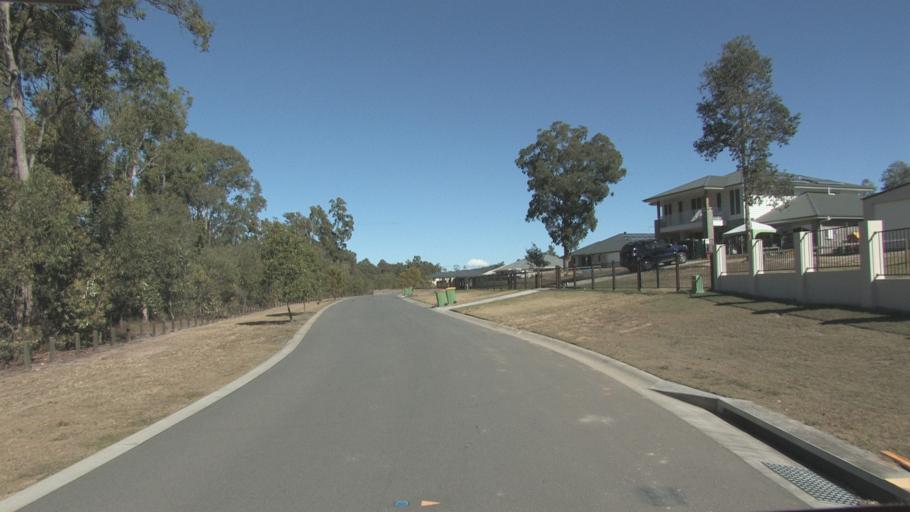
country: AU
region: Queensland
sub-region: Logan
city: North Maclean
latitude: -27.7522
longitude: 152.9542
